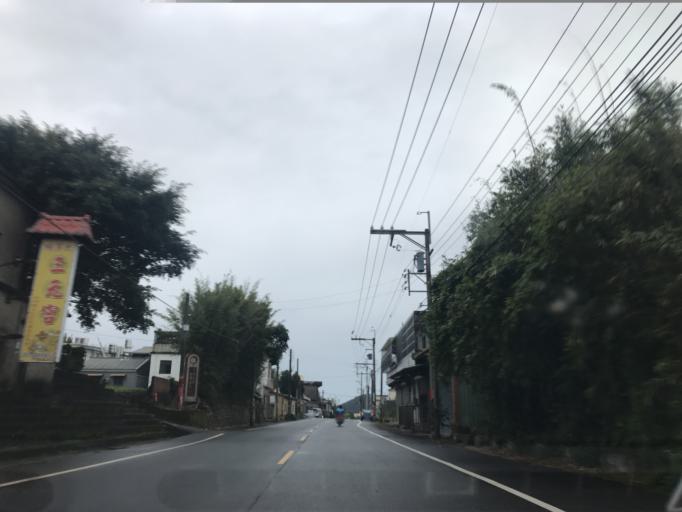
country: TW
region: Taiwan
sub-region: Hsinchu
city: Zhubei
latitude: 24.8408
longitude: 121.1221
